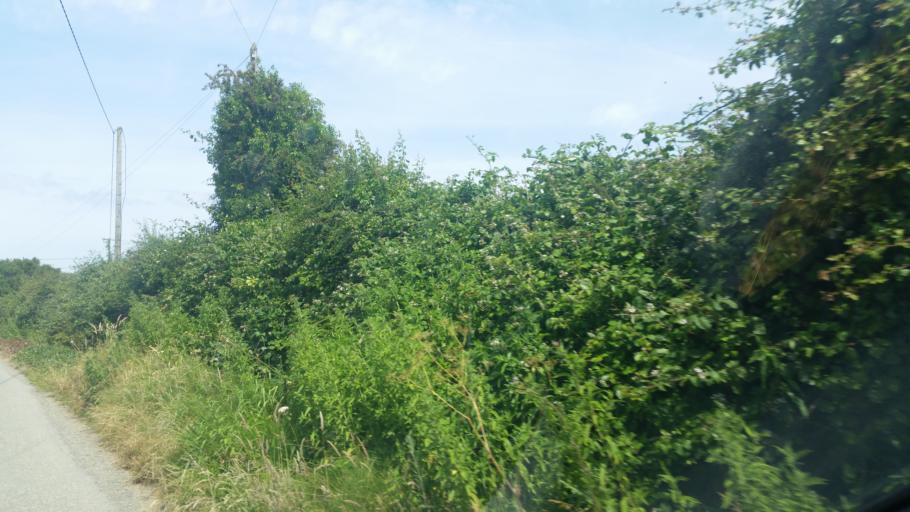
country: IE
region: Leinster
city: Lusk
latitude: 53.5328
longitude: -6.1553
